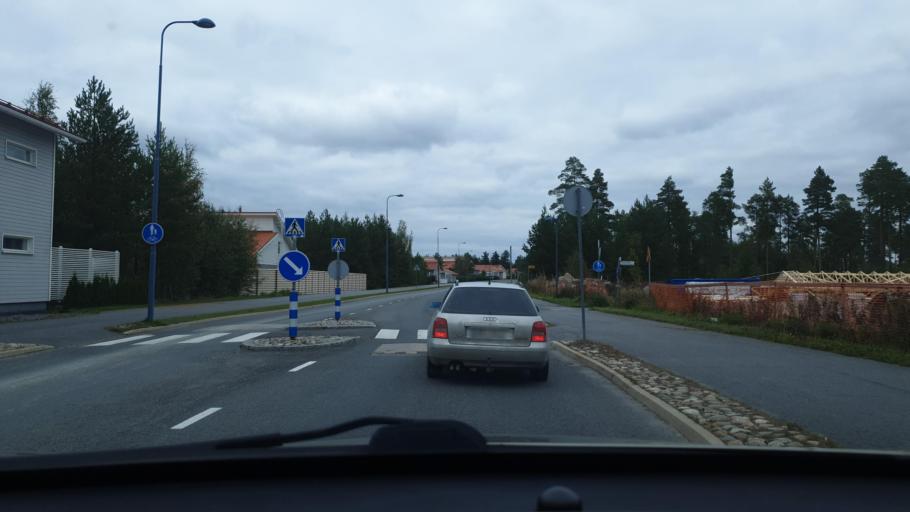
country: FI
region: Ostrobothnia
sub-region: Vaasa
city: Korsholm
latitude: 63.1223
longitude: 21.6573
